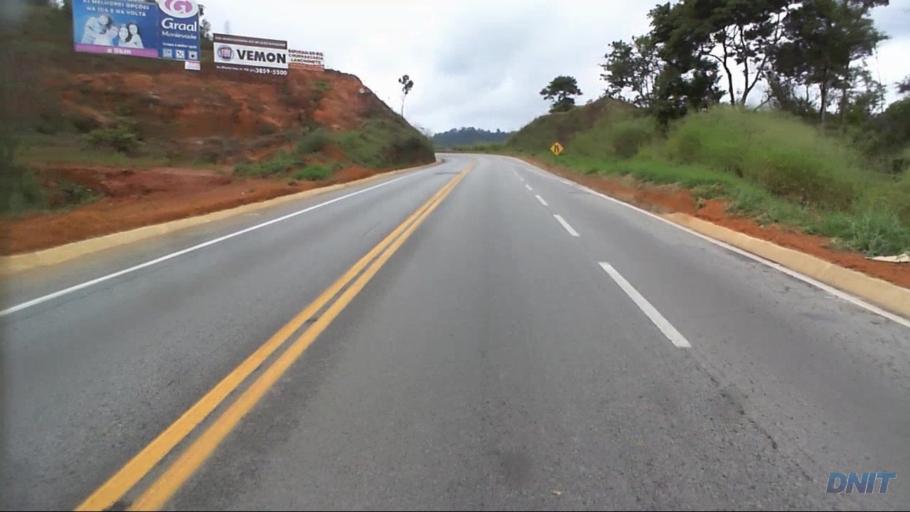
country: BR
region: Minas Gerais
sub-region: Joao Monlevade
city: Joao Monlevade
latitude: -19.8591
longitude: -43.1234
